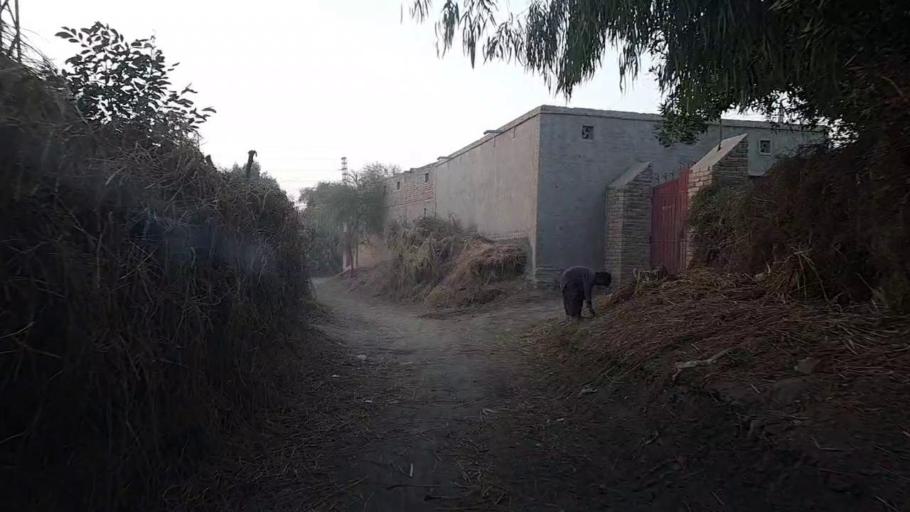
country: PK
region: Sindh
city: Kashmor
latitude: 28.4193
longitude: 69.4488
